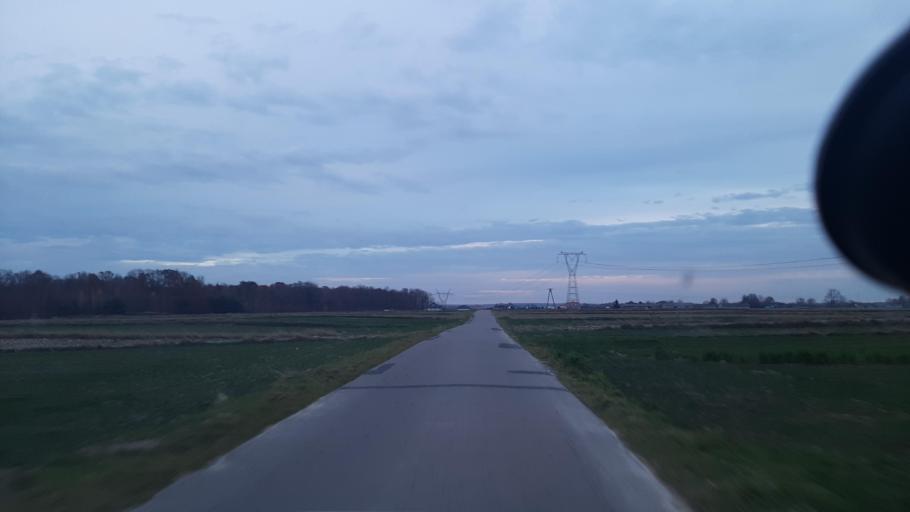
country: PL
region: Lublin Voivodeship
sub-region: Powiat lubelski
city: Garbow
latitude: 51.3731
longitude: 22.3774
